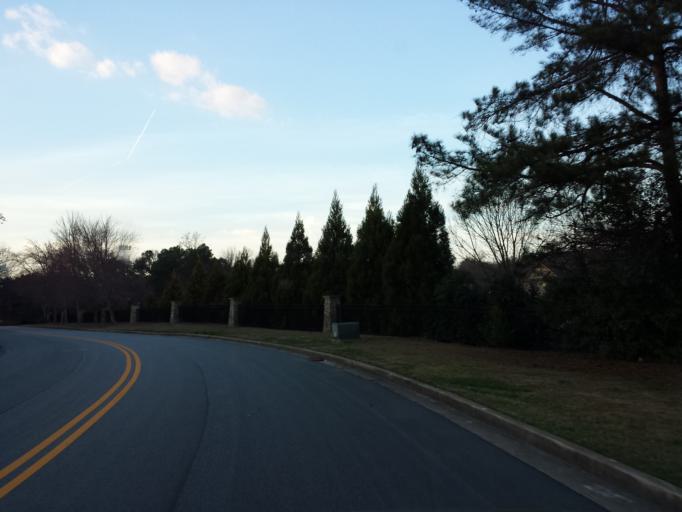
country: US
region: Georgia
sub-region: Cobb County
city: Vinings
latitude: 33.9064
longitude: -84.4741
